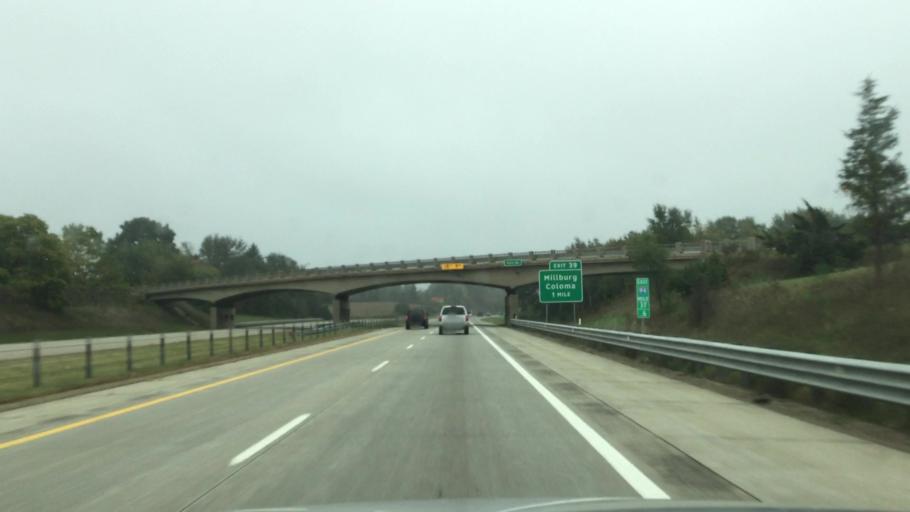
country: US
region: Michigan
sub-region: Berrien County
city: Coloma
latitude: 42.1694
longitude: -86.3210
